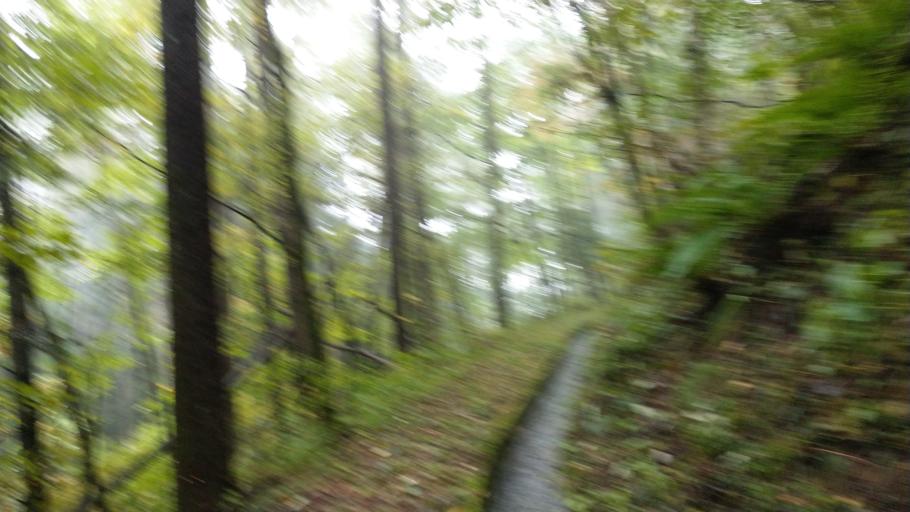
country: JP
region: Nagano
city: Komoro
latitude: 36.3657
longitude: 138.4449
